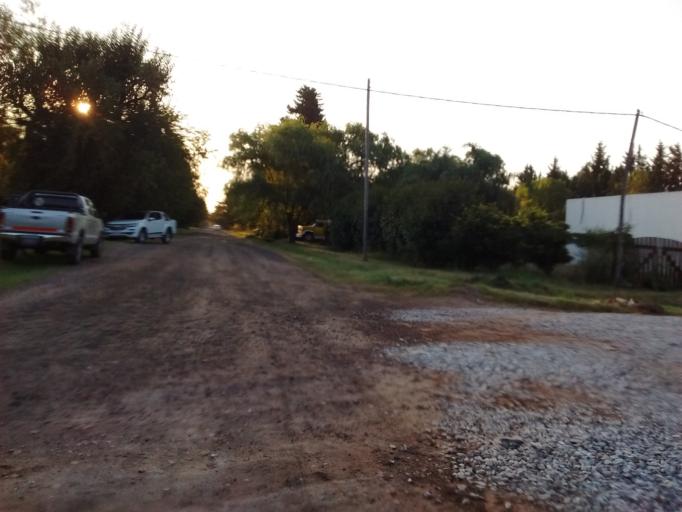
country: AR
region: Santa Fe
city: Funes
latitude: -32.9218
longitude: -60.8324
